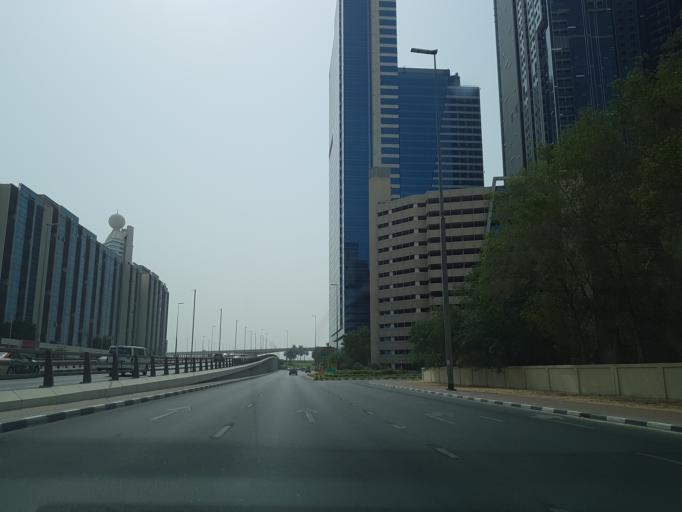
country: AE
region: Ash Shariqah
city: Sharjah
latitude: 25.2314
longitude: 55.2851
